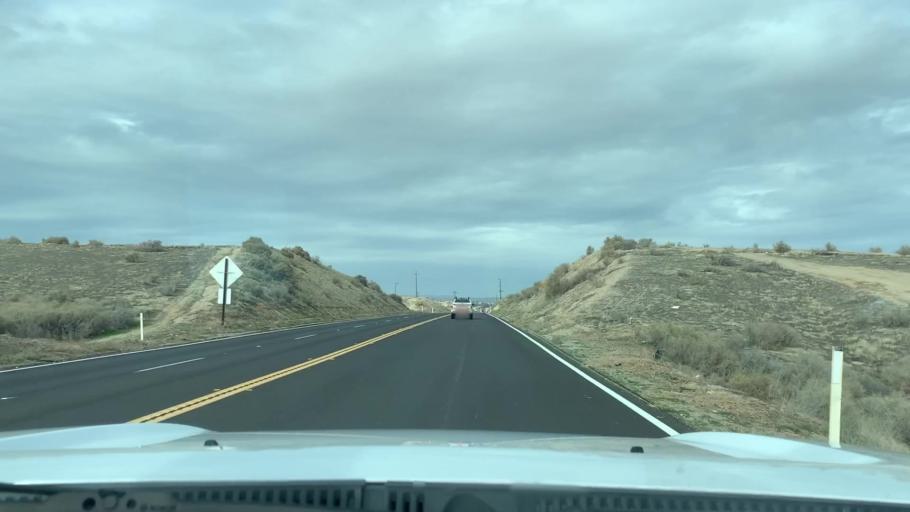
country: US
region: California
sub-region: Kern County
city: South Taft
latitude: 35.1198
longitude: -119.4340
